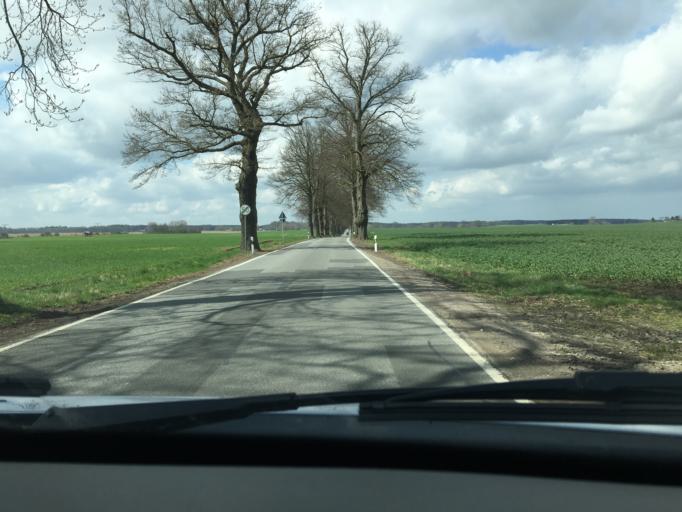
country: DE
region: Mecklenburg-Vorpommern
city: Bad Sulze
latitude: 54.1768
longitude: 12.6478
